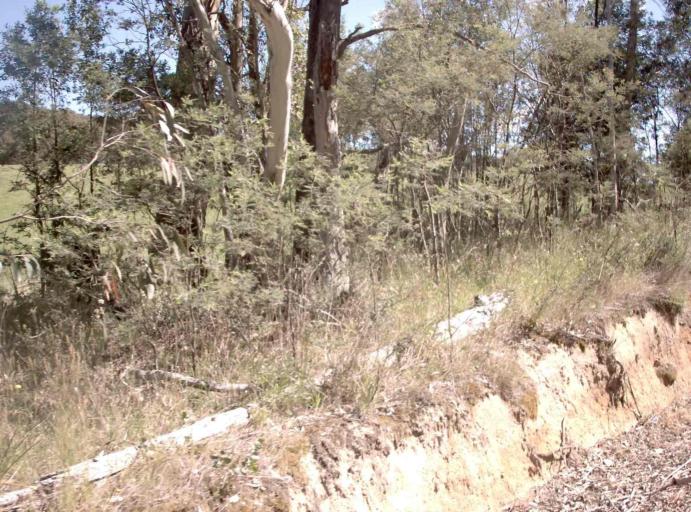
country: AU
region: New South Wales
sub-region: Bombala
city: Bombala
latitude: -37.0579
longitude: 148.8029
